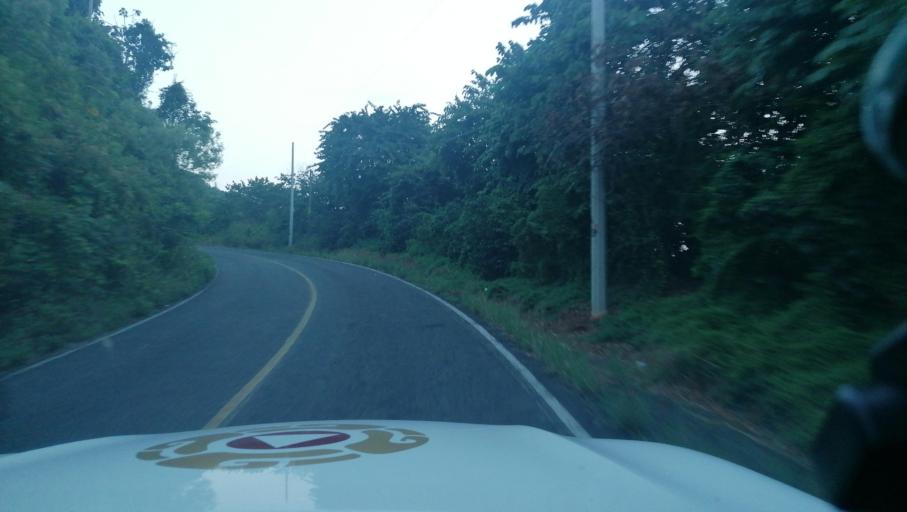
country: MX
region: Chiapas
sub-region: Cacahoatan
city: Benito Juarez
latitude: 15.0443
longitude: -92.2451
